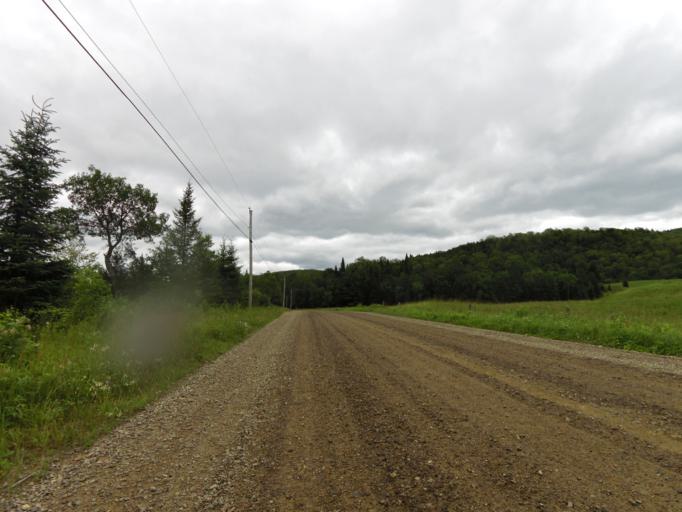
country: CA
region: Ontario
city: Hawkesbury
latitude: 45.8958
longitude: -74.6571
